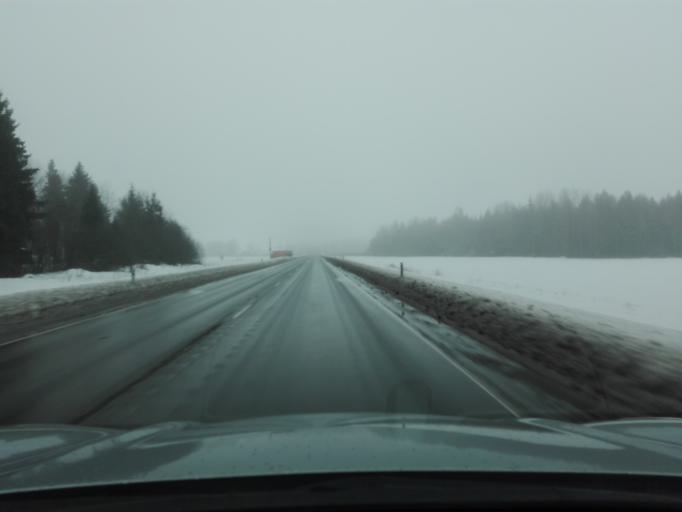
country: EE
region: Raplamaa
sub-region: Kohila vald
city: Kohila
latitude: 59.2229
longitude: 24.7769
